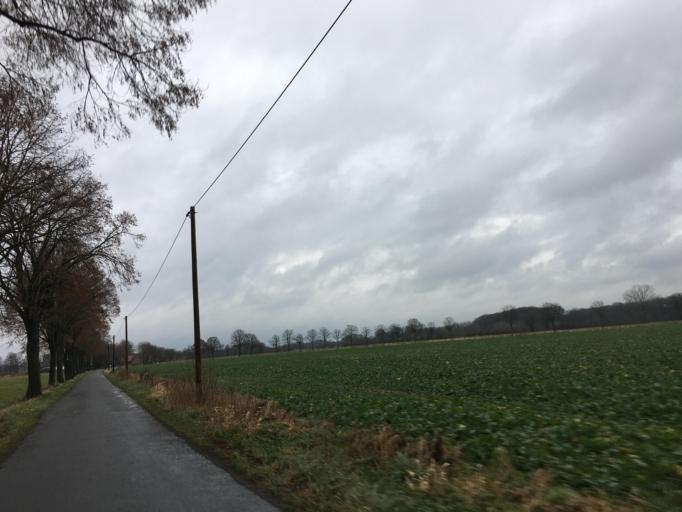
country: DE
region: North Rhine-Westphalia
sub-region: Regierungsbezirk Munster
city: Nordwalde
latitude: 52.0980
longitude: 7.4794
